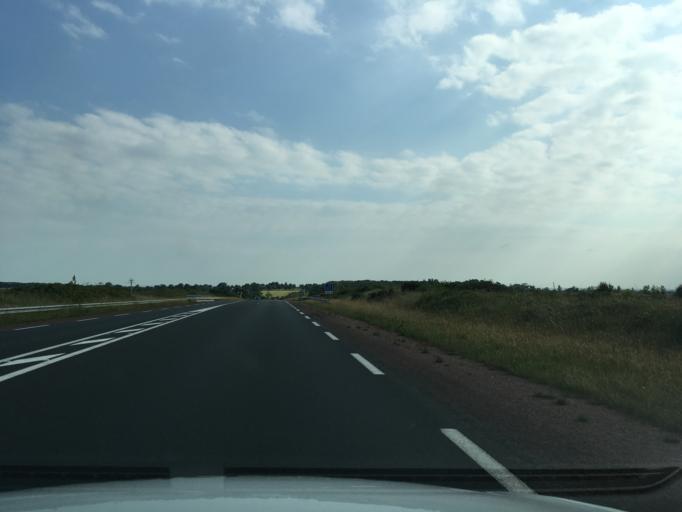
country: FR
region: Poitou-Charentes
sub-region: Departement des Deux-Sevres
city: Saint-Pardoux
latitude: 46.5185
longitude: -0.3289
